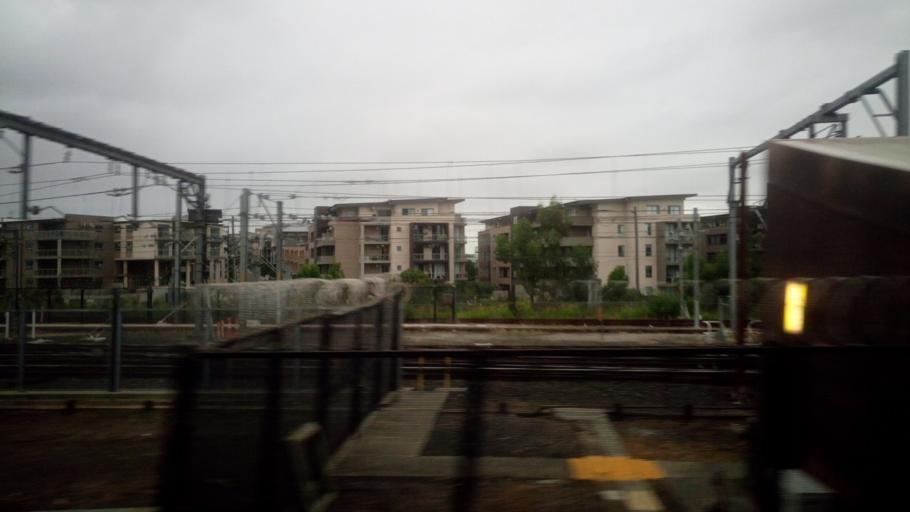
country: AU
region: New South Wales
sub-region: Strathfield
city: Homebush
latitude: -33.8638
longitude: 151.0631
